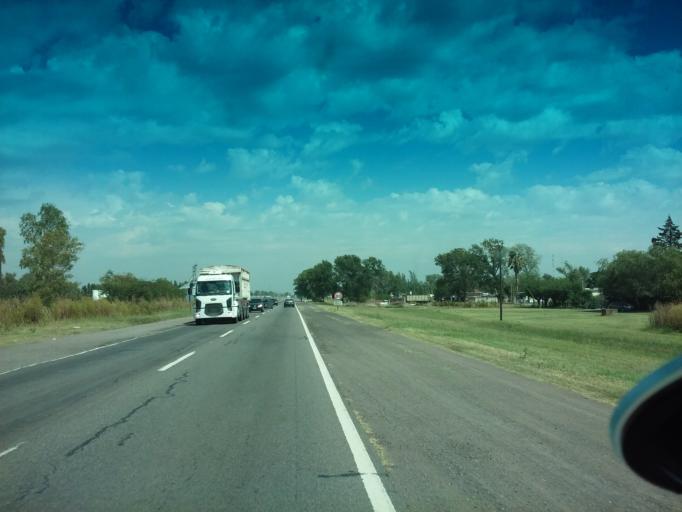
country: AR
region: Buenos Aires
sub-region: Partido de Carlos Casares
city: Carlos Casares
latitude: -35.6312
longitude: -61.3409
